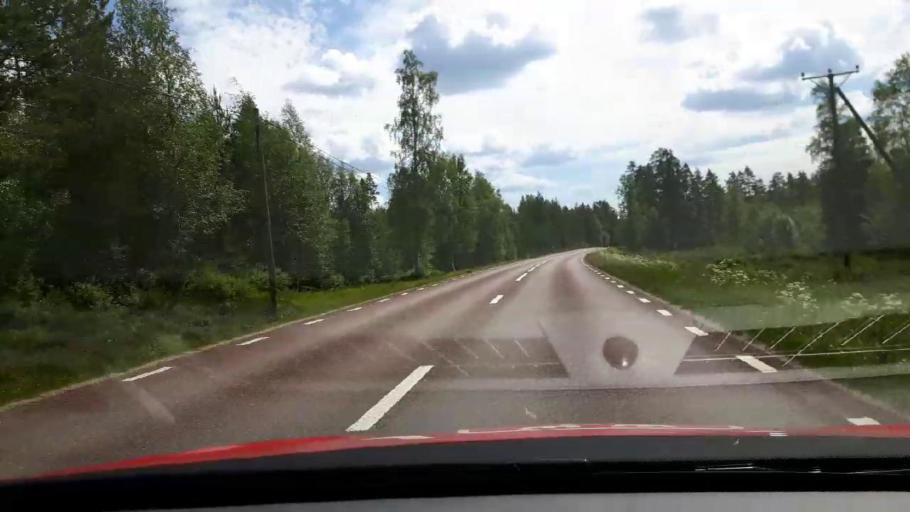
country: SE
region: Jaemtland
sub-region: Harjedalens Kommun
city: Sveg
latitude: 62.1384
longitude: 14.9661
